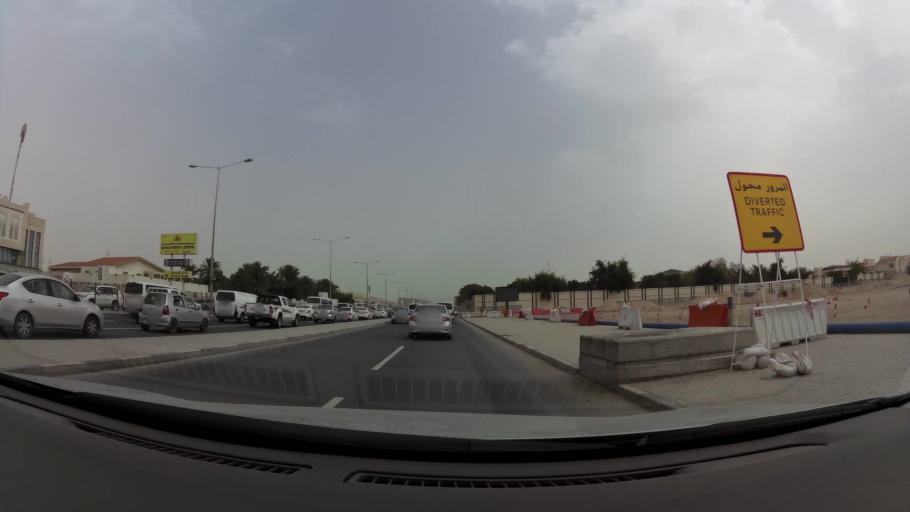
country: QA
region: Baladiyat ad Dawhah
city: Doha
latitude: 25.2668
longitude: 51.5020
